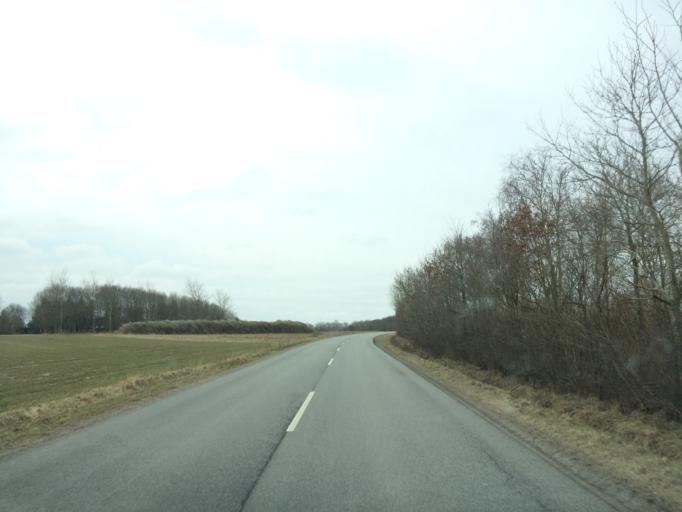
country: DK
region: Central Jutland
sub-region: Ringkobing-Skjern Kommune
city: Tarm
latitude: 55.8258
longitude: 8.4223
